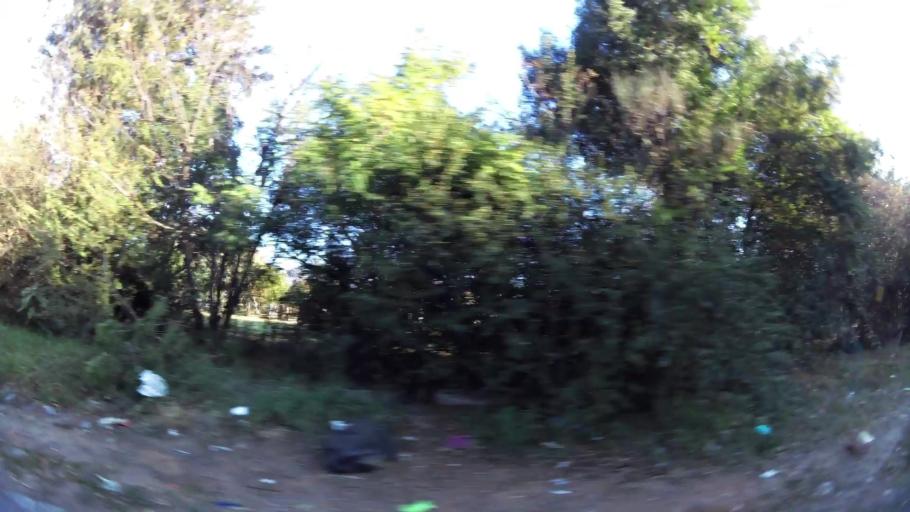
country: ZA
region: Gauteng
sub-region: City of Johannesburg Metropolitan Municipality
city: Midrand
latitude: -26.0245
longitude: 28.1305
